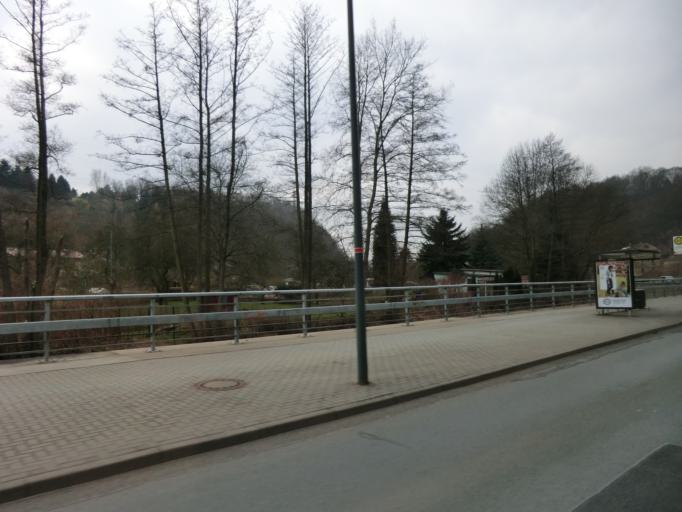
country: DE
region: Saxony
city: Freital
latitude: 51.0209
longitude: 13.6821
